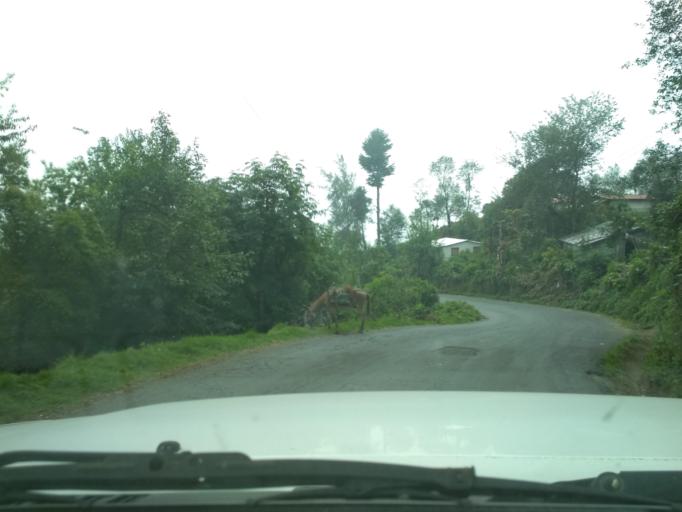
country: MX
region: Veracruz
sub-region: La Perla
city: Metlac Hernandez (Metlac Primero)
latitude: 18.9639
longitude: -97.1667
